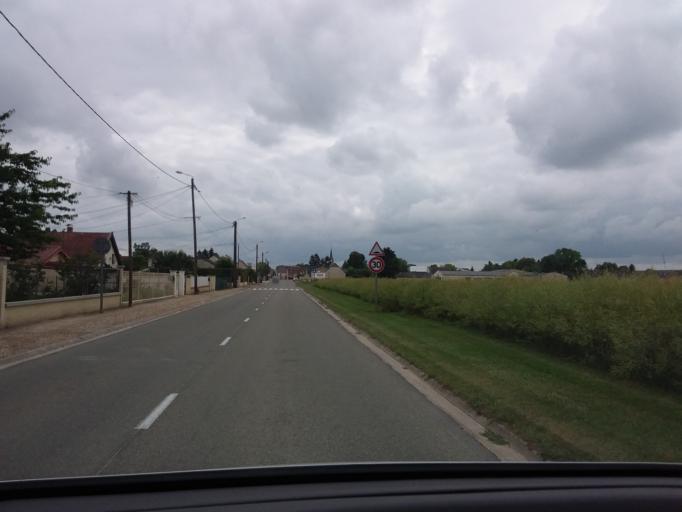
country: FR
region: Champagne-Ardenne
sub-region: Departement de la Marne
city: Cormicy
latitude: 49.4077
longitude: 3.8151
